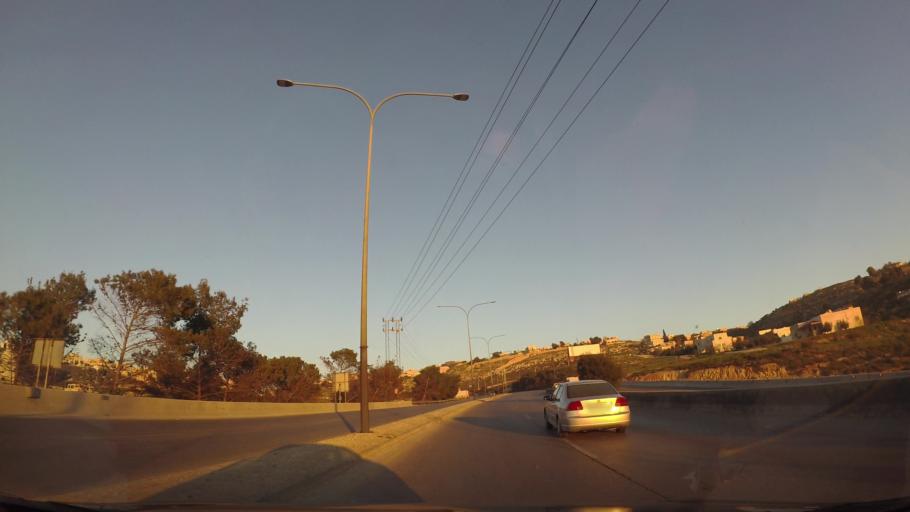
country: JO
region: Amman
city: Umm as Summaq
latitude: 31.8605
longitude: 35.8078
